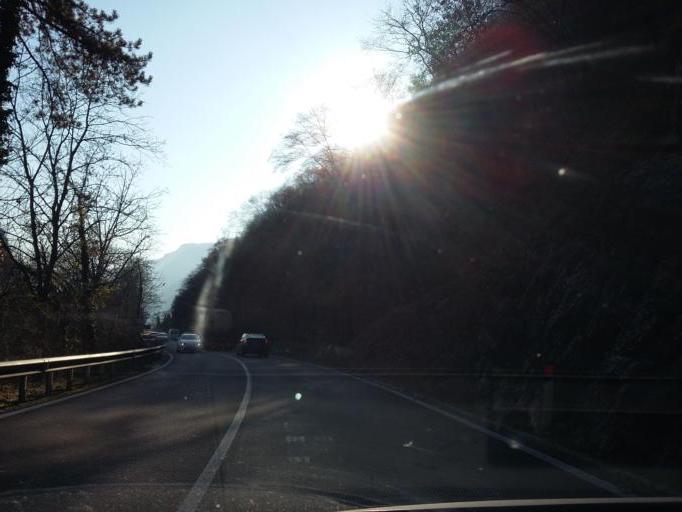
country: IT
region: Trentino-Alto Adige
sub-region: Provincia di Trento
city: Nago-Torbole
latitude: 45.8661
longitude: 10.9148
